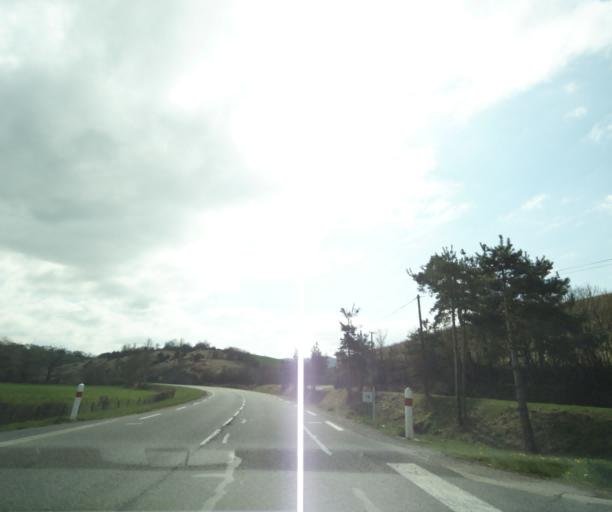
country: FR
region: Midi-Pyrenees
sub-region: Departement de l'Aveyron
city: Laissac
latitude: 44.3550
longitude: 2.9085
